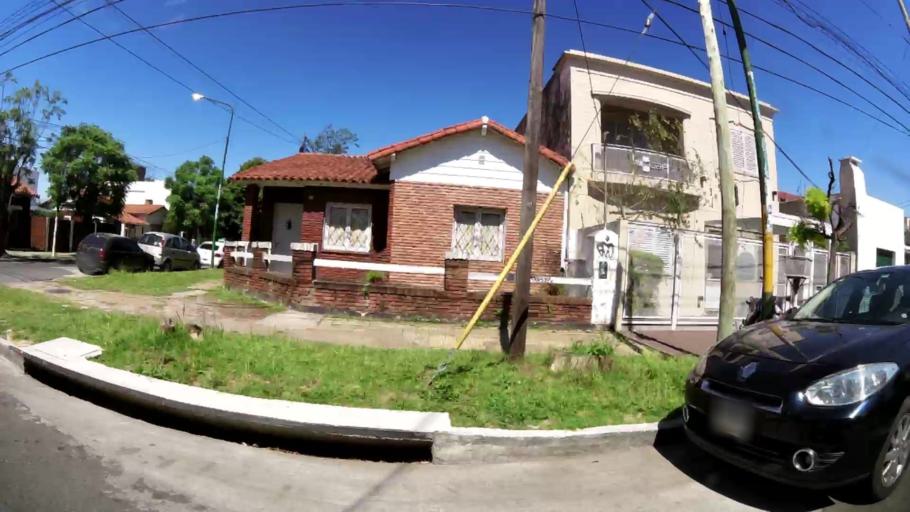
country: AR
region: Buenos Aires
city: Ituzaingo
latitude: -34.6553
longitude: -58.6661
